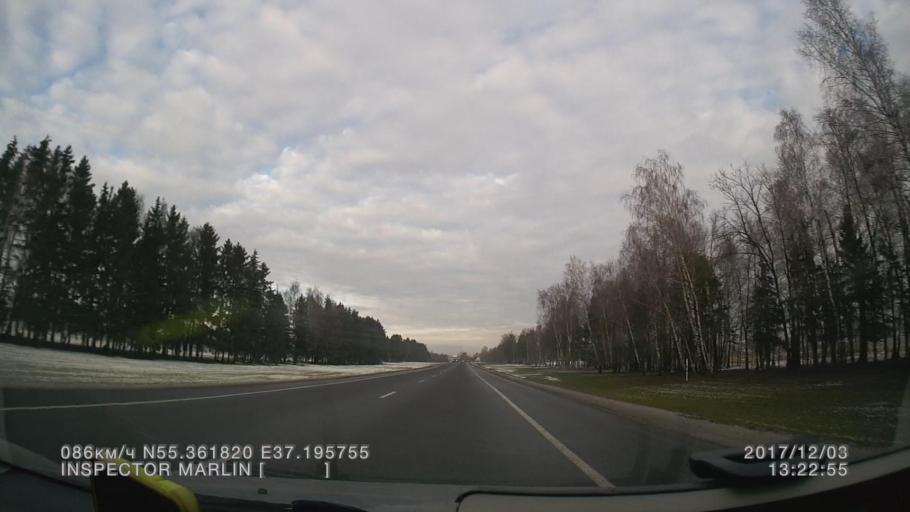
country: RU
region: Moskovskaya
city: Troitsk
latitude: 55.3619
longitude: 37.1958
